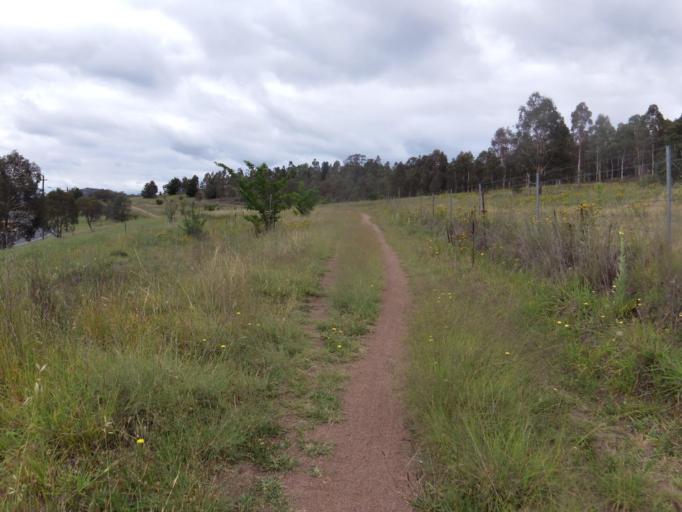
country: AU
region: Australian Capital Territory
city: Macquarie
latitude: -35.3371
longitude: 149.0260
